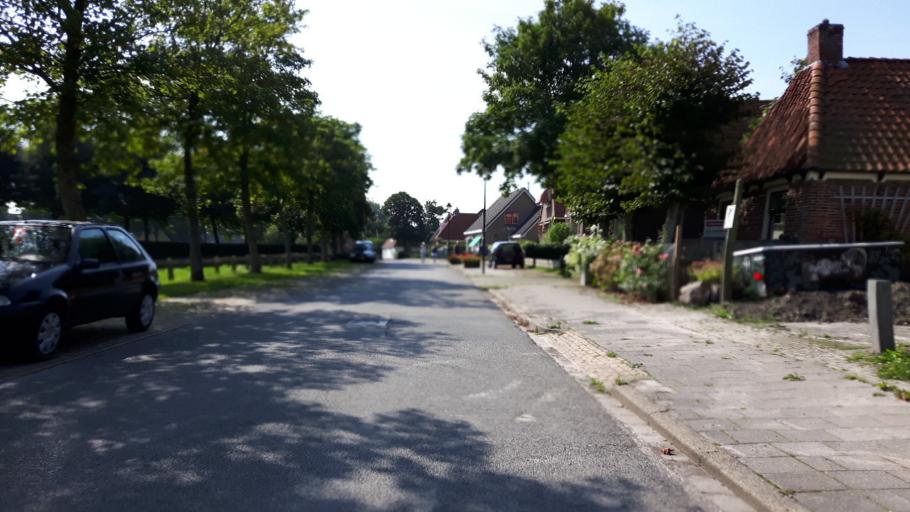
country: NL
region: Friesland
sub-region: Gemeente Ferwerderadiel
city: Hallum
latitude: 53.2926
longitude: 5.7668
